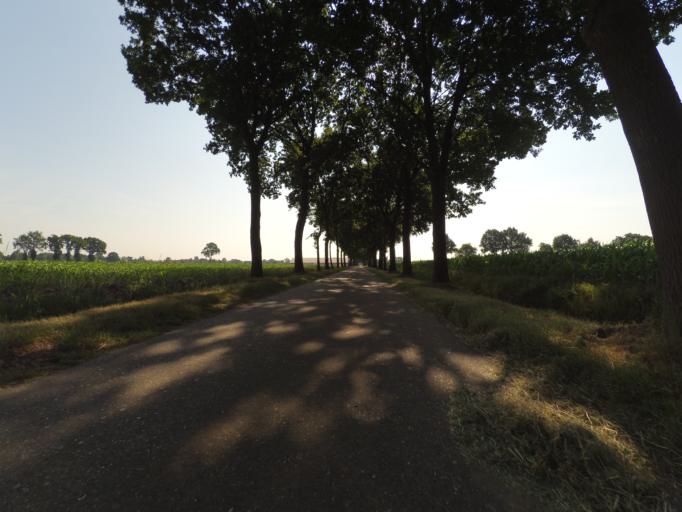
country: BE
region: Flanders
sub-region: Provincie Antwerpen
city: Essen
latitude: 51.4487
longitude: 4.4825
